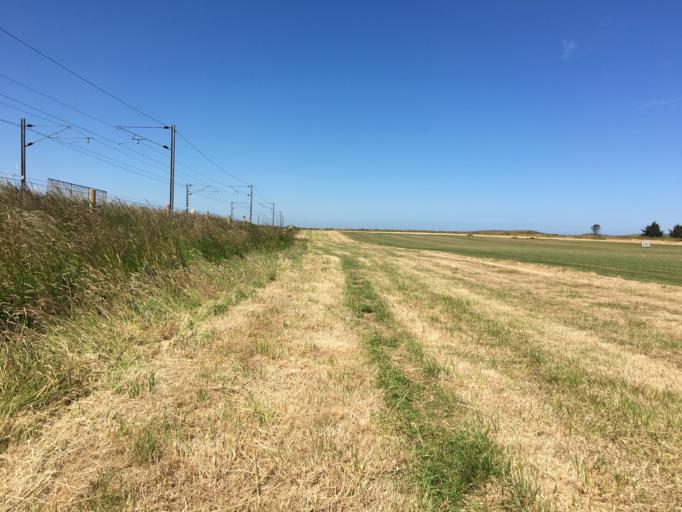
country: GB
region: England
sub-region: Northumberland
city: Ancroft
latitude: 55.7077
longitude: -1.9297
